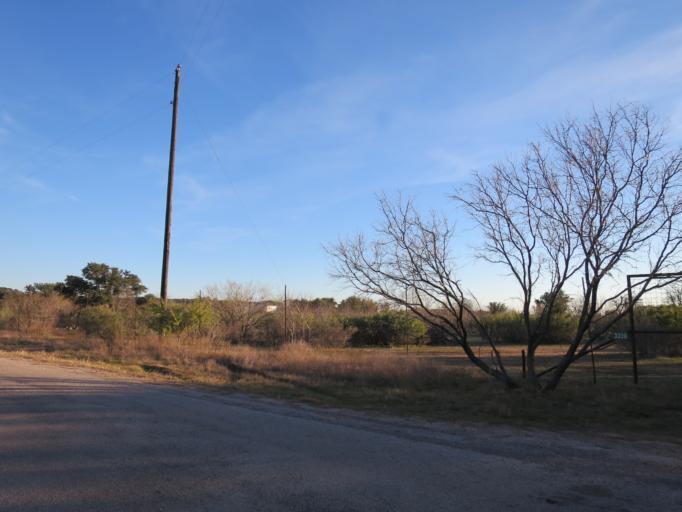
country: US
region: Texas
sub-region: Burnet County
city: Marble Falls
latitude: 30.6190
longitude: -98.2253
